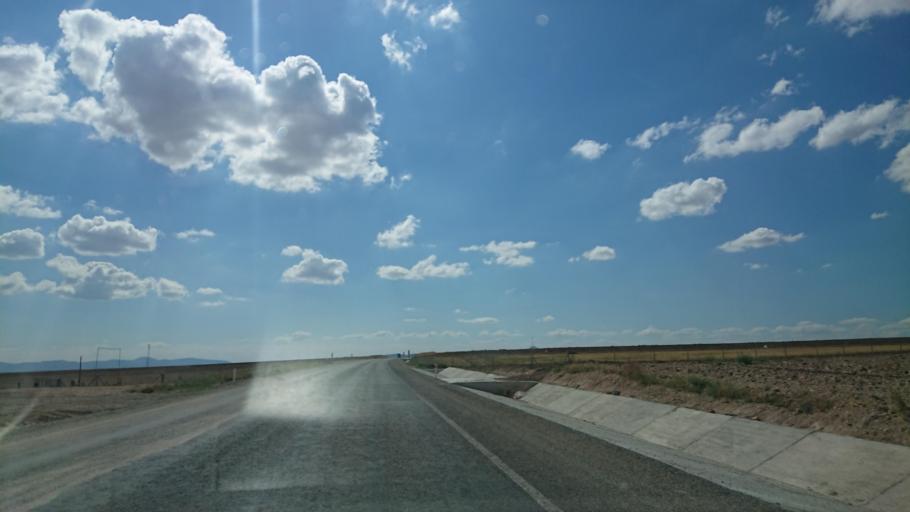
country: TR
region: Kirsehir
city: Kirsehir
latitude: 39.1219
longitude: 34.0089
